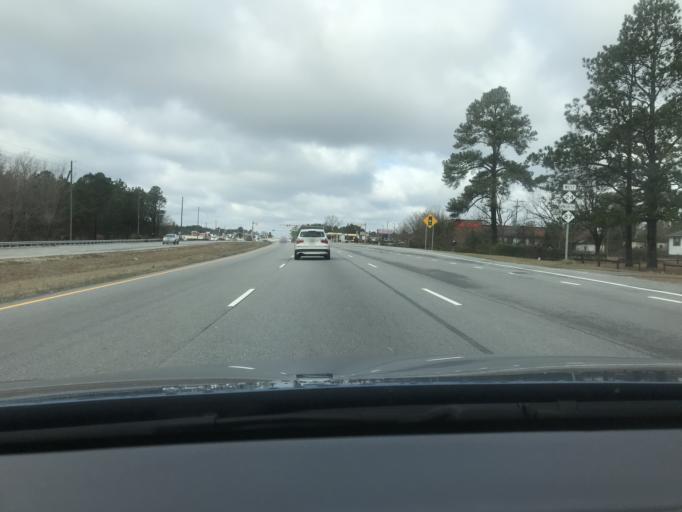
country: US
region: North Carolina
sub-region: Cumberland County
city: Spring Lake
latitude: 35.2525
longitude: -79.0284
